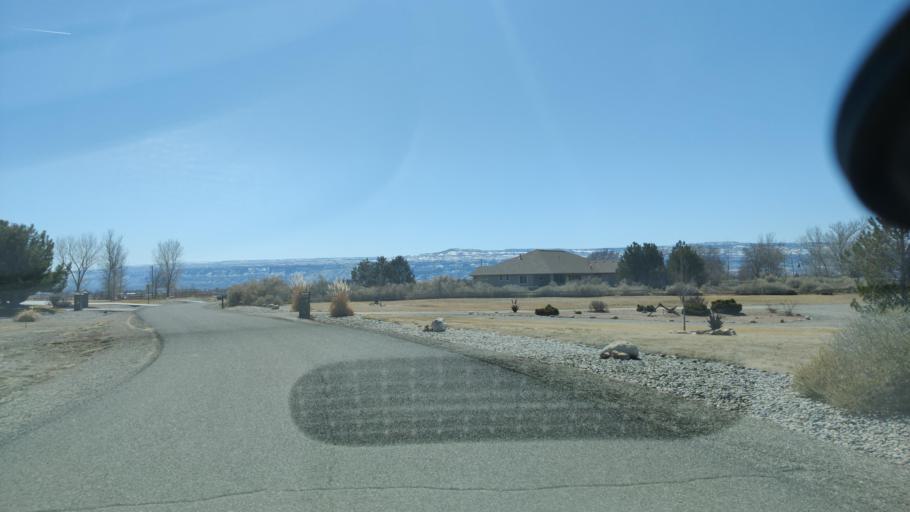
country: US
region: Colorado
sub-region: Mesa County
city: Fruita
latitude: 39.2057
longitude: -108.7137
